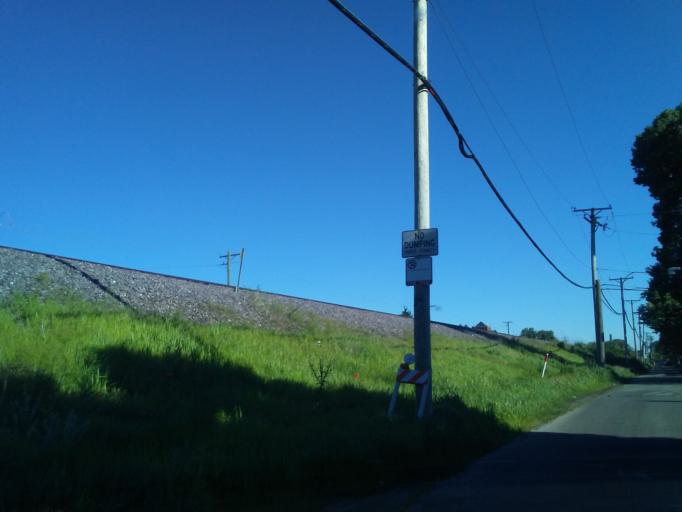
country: US
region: Illinois
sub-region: Cook County
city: Oak Park
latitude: 41.9272
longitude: -87.7419
